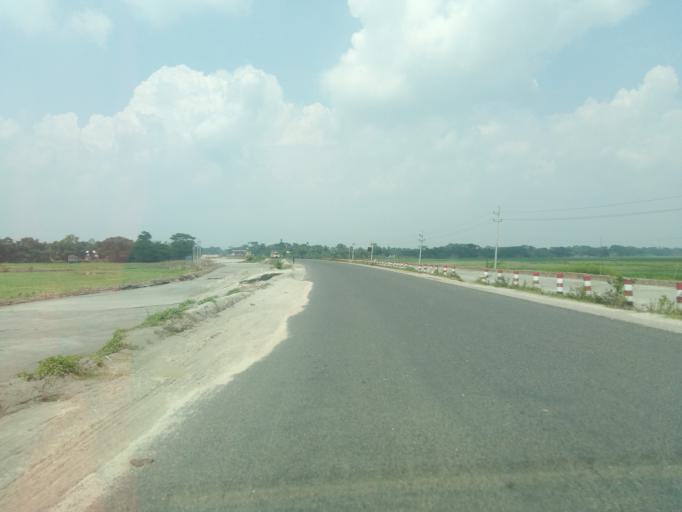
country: BD
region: Dhaka
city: Char Bhadrasan
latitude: 23.3851
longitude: 90.1258
